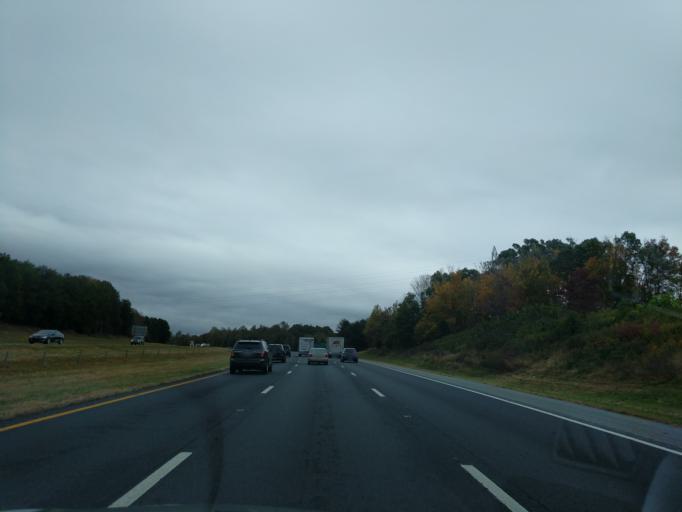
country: US
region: North Carolina
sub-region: Davidson County
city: Thomasville
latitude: 35.8589
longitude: -80.0610
